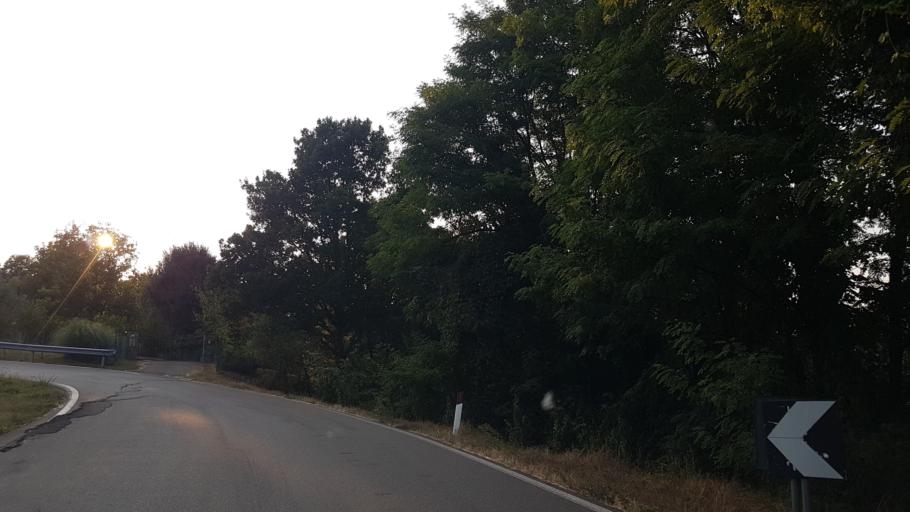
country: IT
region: Emilia-Romagna
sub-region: Provincia di Parma
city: Albareto
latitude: 44.4757
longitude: 9.7074
